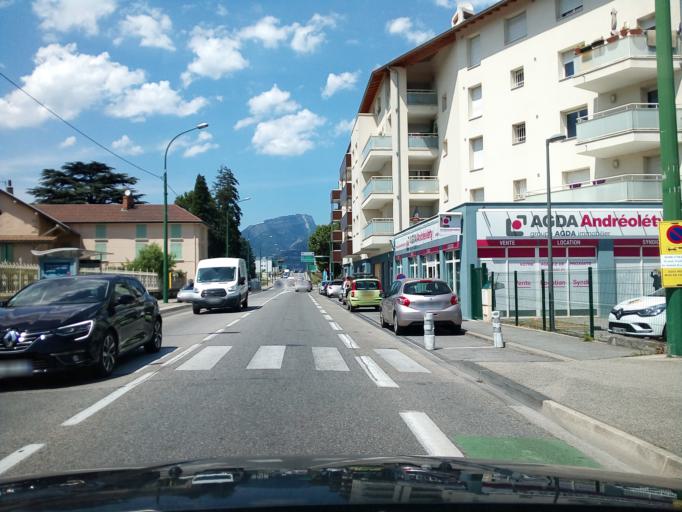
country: FR
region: Rhone-Alpes
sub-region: Departement de l'Isere
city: Eybens
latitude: 45.1535
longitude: 5.7484
